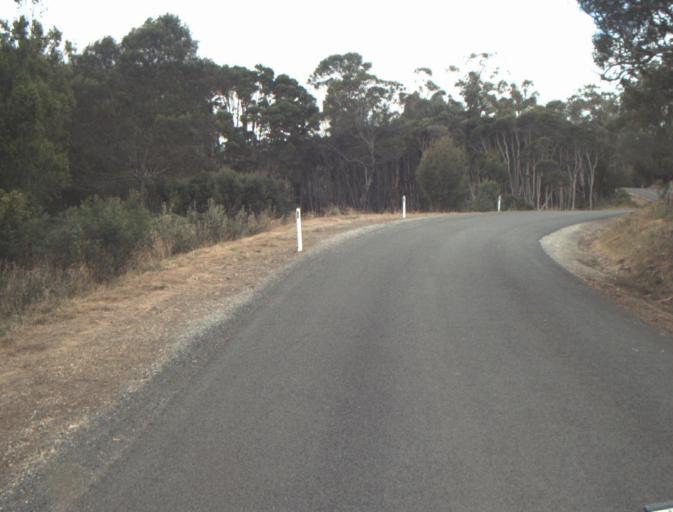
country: AU
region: Tasmania
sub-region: Launceston
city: Mayfield
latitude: -41.2838
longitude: 147.0145
